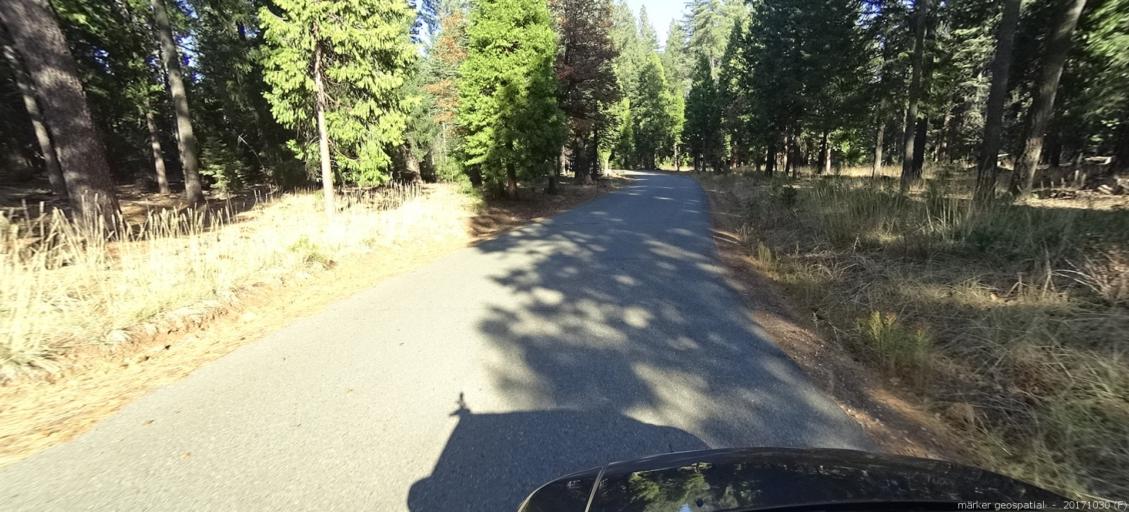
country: US
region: California
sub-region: Shasta County
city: Shingletown
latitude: 40.5395
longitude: -121.7385
